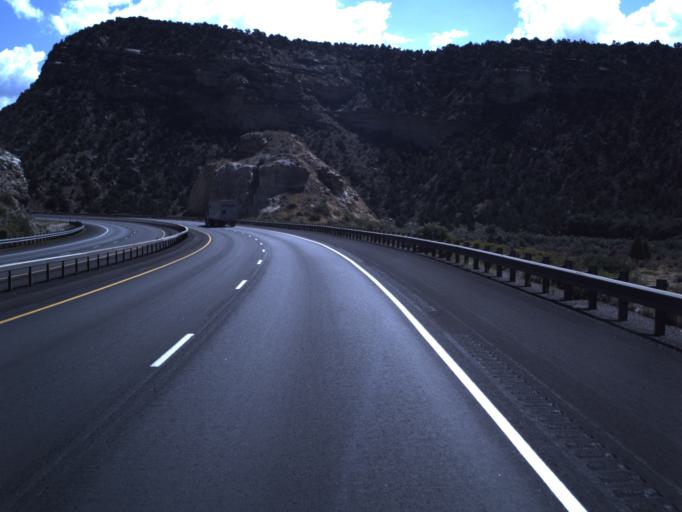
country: US
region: Utah
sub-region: Sevier County
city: Salina
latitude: 38.9107
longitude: -111.7114
